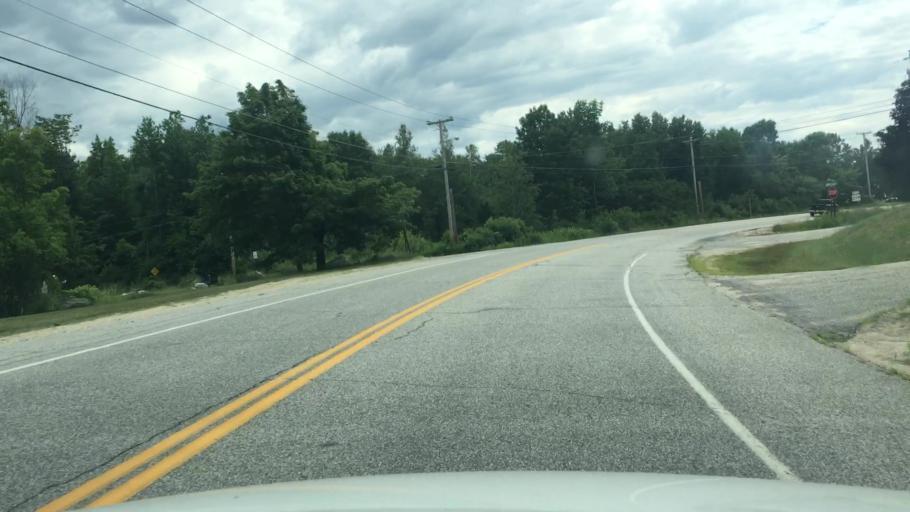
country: US
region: Maine
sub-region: Oxford County
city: West Paris
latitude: 44.3394
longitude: -70.5310
